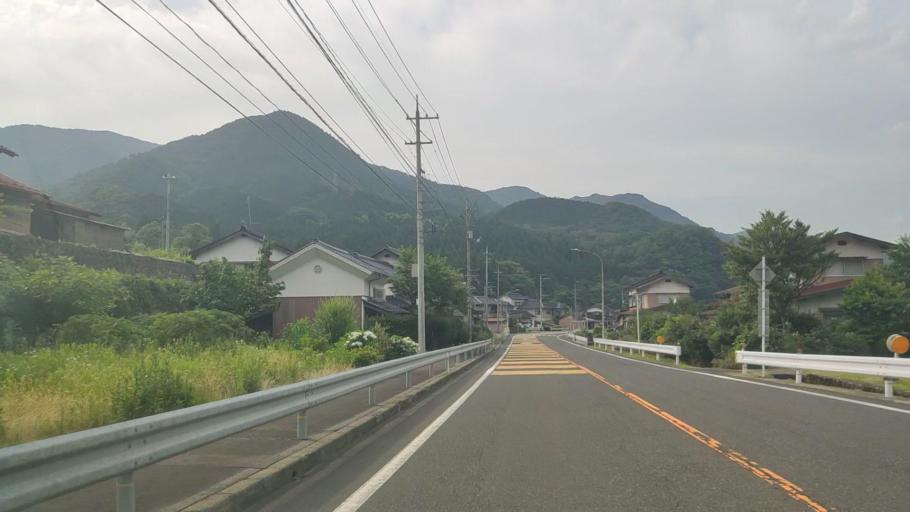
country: JP
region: Tottori
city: Kurayoshi
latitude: 35.3368
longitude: 133.8412
